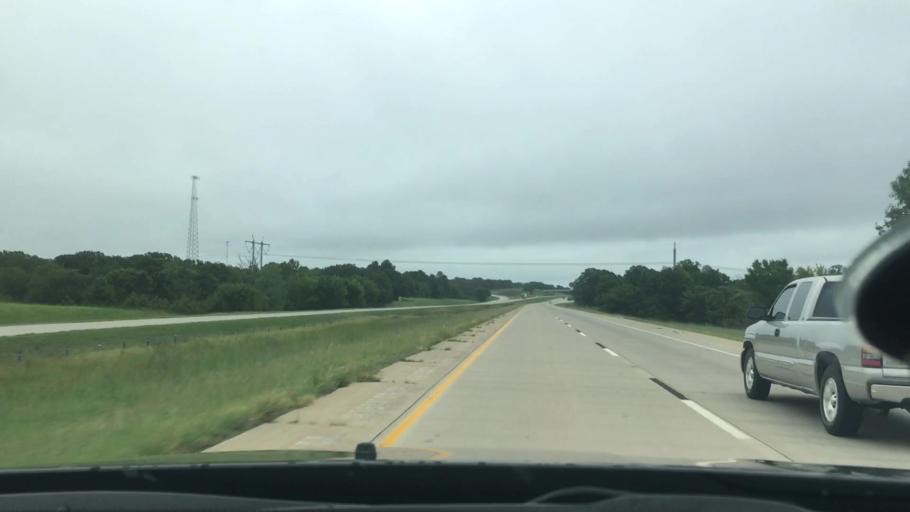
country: US
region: Oklahoma
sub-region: Okfuskee County
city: Okemah
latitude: 35.4293
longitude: -96.2059
